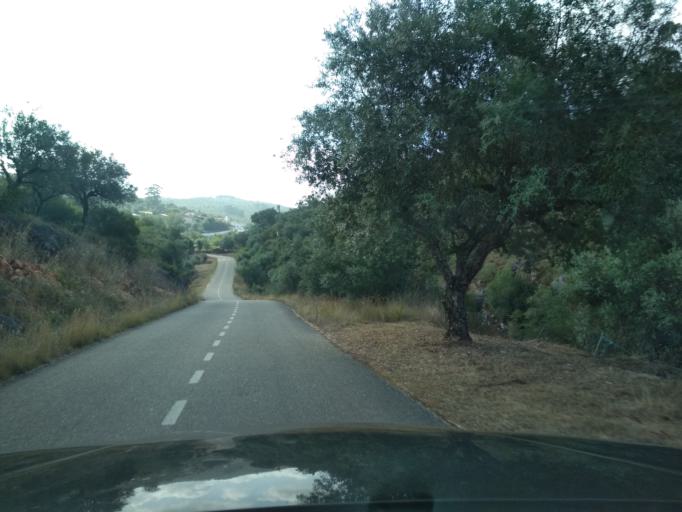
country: PT
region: Coimbra
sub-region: Condeixa-A-Nova
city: Condeixa-a-Nova
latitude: 40.0726
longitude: -8.5020
